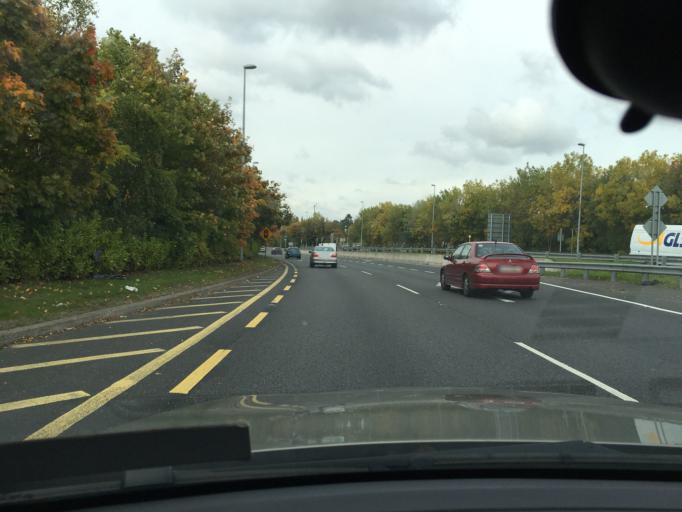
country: IE
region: Leinster
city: Castleknock
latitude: 53.3832
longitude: -6.3648
